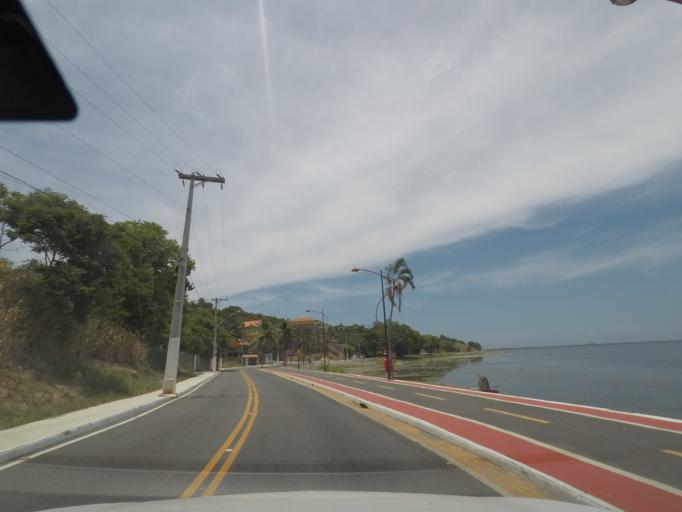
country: BR
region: Rio de Janeiro
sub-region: Marica
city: Marica
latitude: -22.9293
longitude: -42.8267
